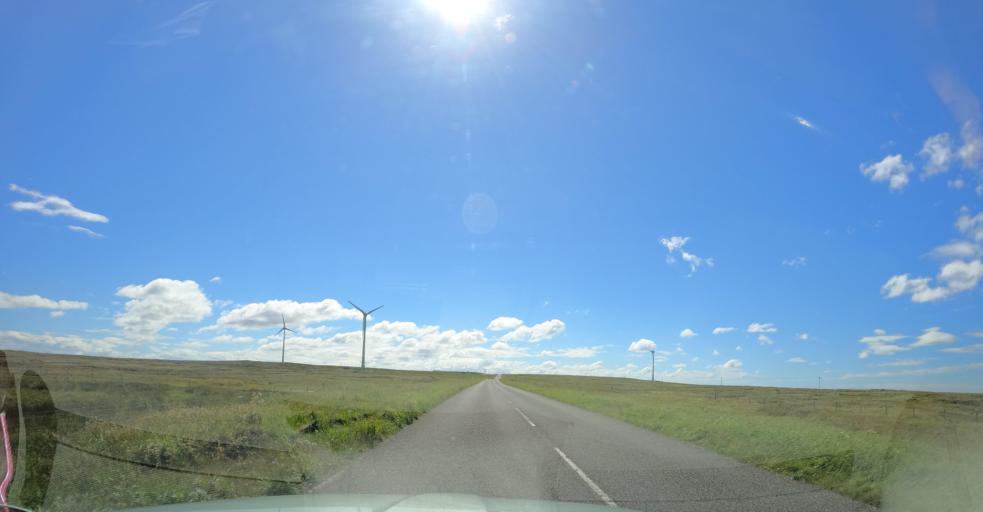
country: GB
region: Scotland
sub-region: Eilean Siar
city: Isle of Lewis
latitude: 58.3875
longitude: -6.4916
